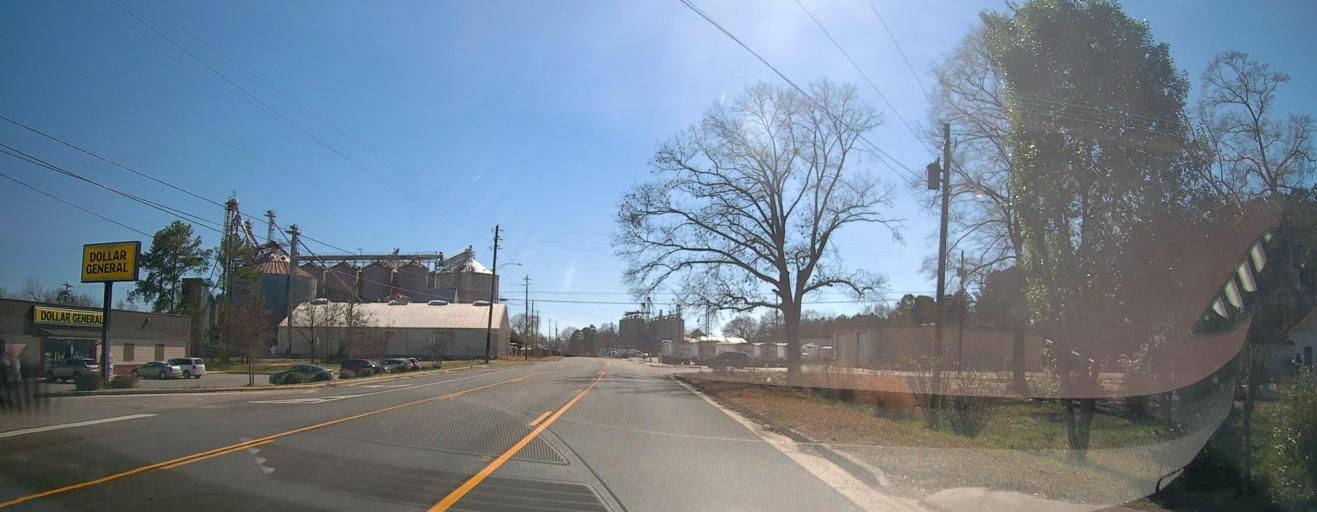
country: US
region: Georgia
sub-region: Macon County
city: Marshallville
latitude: 32.4615
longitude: -83.9401
